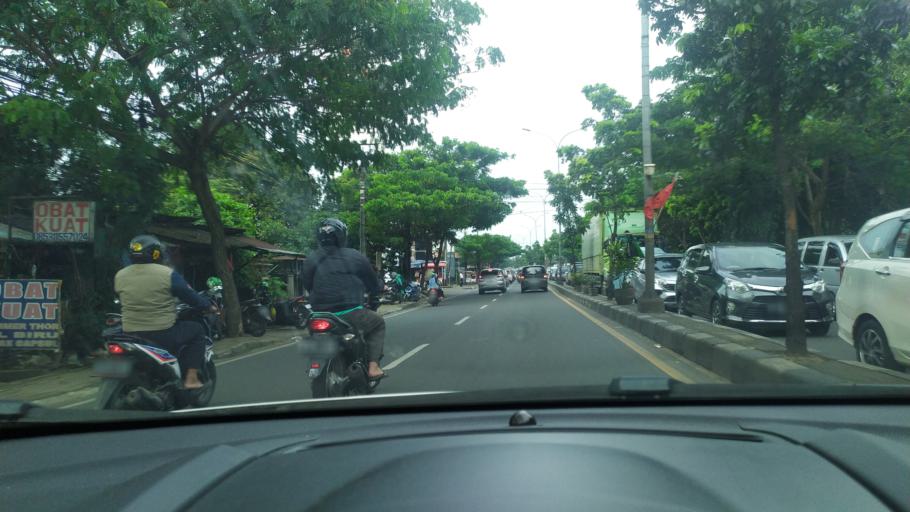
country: ID
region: Banten
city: South Tangerang
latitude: -6.3030
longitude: 106.7600
